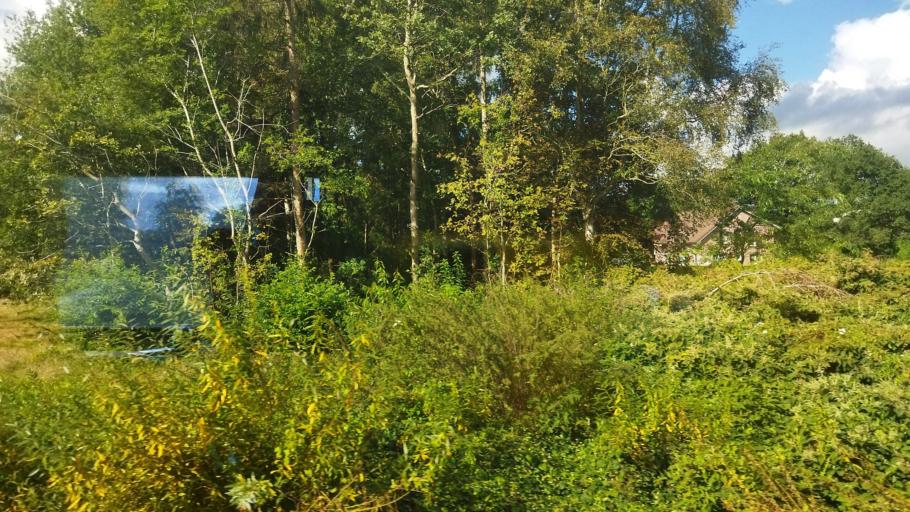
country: DE
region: Lower Saxony
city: Papenburg
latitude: 53.1030
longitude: 7.4053
